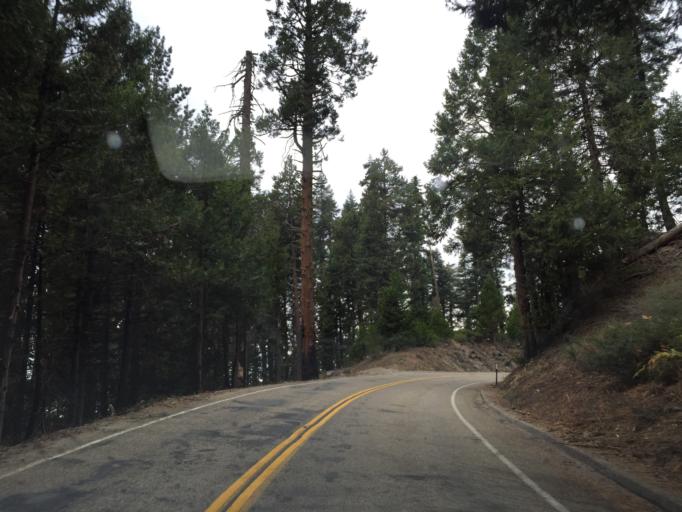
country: US
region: California
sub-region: Tulare County
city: Three Rivers
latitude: 36.7179
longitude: -118.9428
